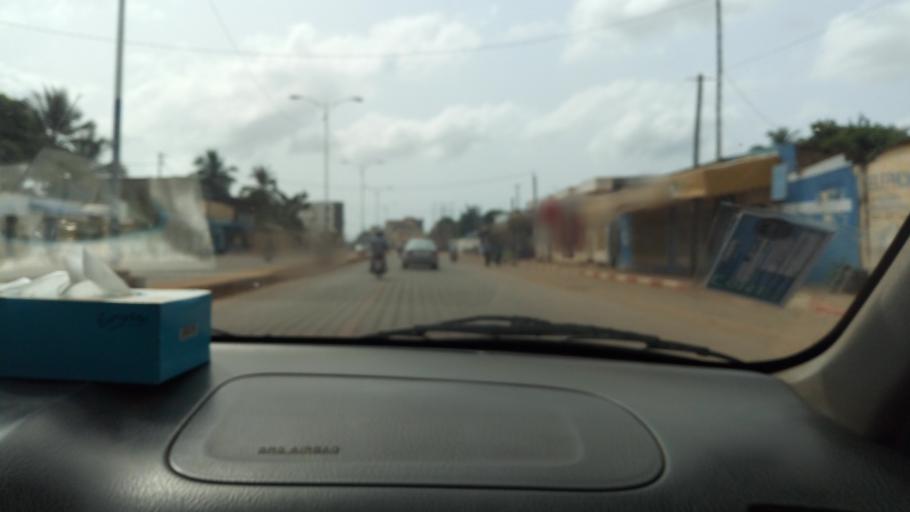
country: TG
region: Maritime
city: Lome
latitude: 6.1819
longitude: 1.1949
